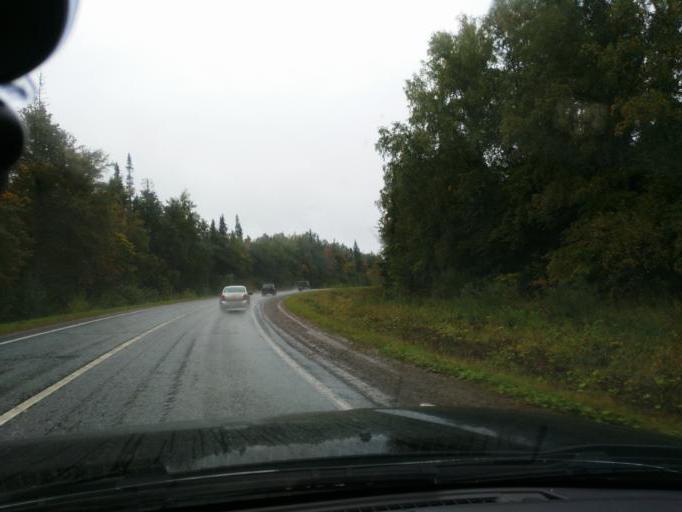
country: RU
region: Perm
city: Yugo-Kamskiy
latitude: 57.5995
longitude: 55.6533
